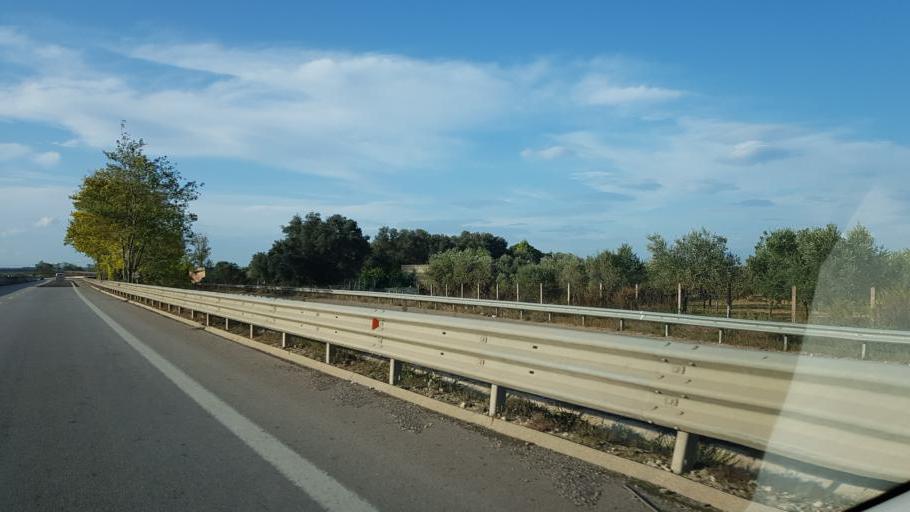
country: IT
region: Apulia
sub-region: Provincia di Brindisi
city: Francavilla Fontana
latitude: 40.5388
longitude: 17.6073
